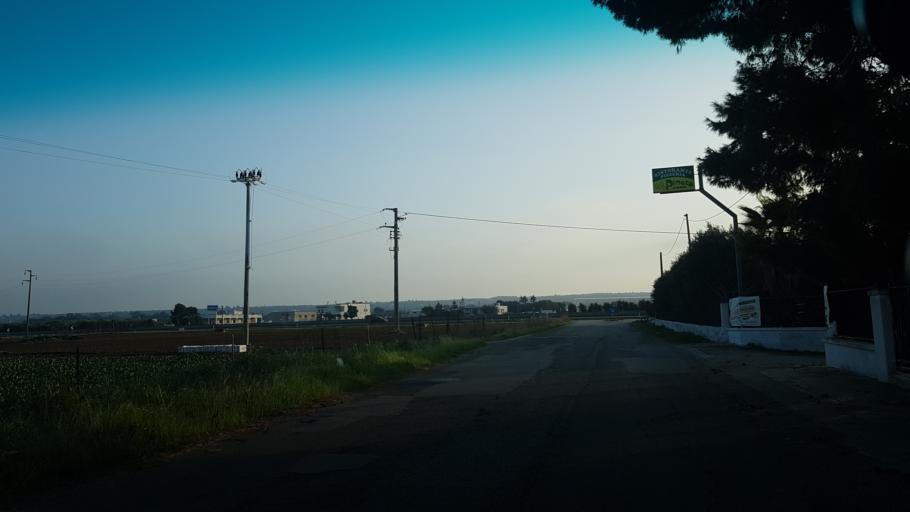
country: IT
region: Apulia
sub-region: Provincia di Brindisi
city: Carovigno
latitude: 40.7443
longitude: 17.7144
